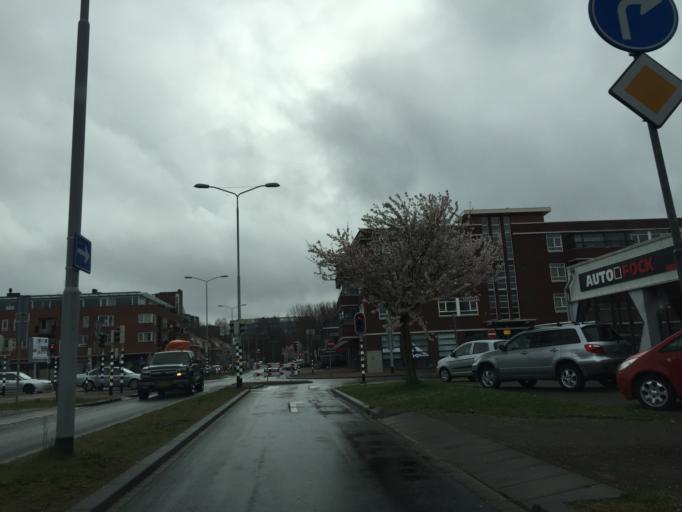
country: NL
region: South Holland
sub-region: Gemeente Leidschendam-Voorburg
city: Voorburg
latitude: 52.0840
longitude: 4.3955
